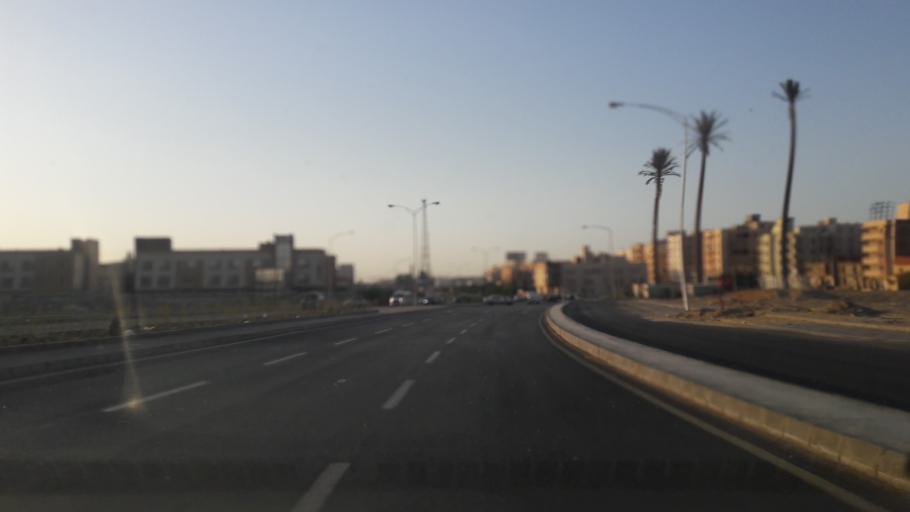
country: EG
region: Al Jizah
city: Madinat Sittah Uktubar
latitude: 29.9555
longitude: 30.9337
